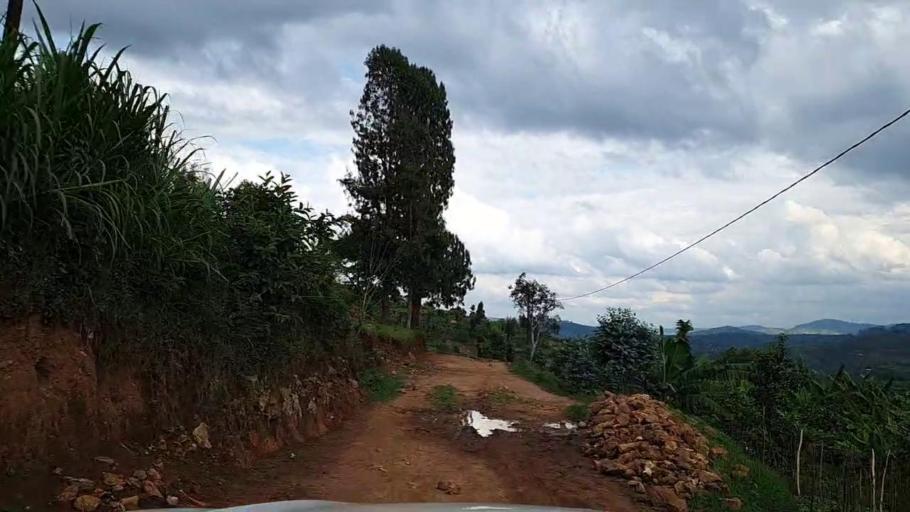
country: RW
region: Southern Province
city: Gikongoro
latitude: -2.4349
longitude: 29.6369
